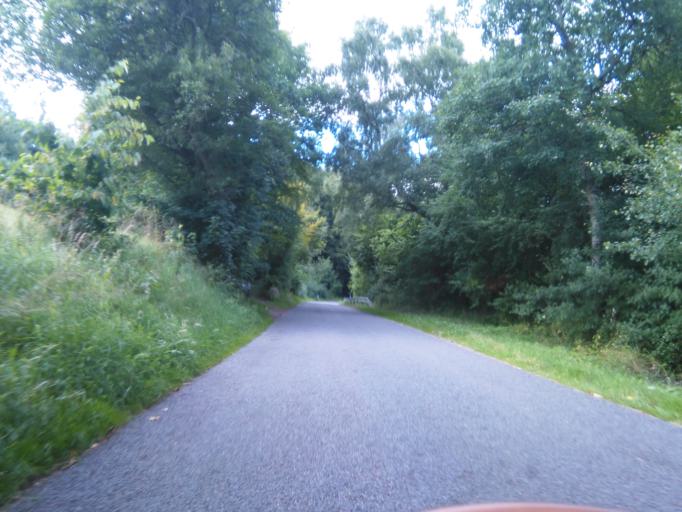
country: DK
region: Central Jutland
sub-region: Skanderborg Kommune
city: Horning
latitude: 56.1005
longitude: 10.0188
